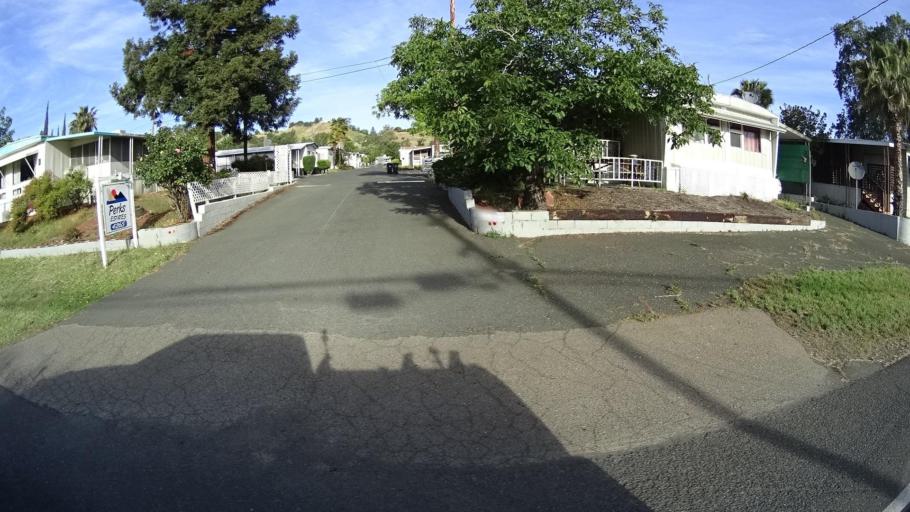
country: US
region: California
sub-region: Lake County
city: North Lakeport
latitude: 39.0929
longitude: -122.9028
